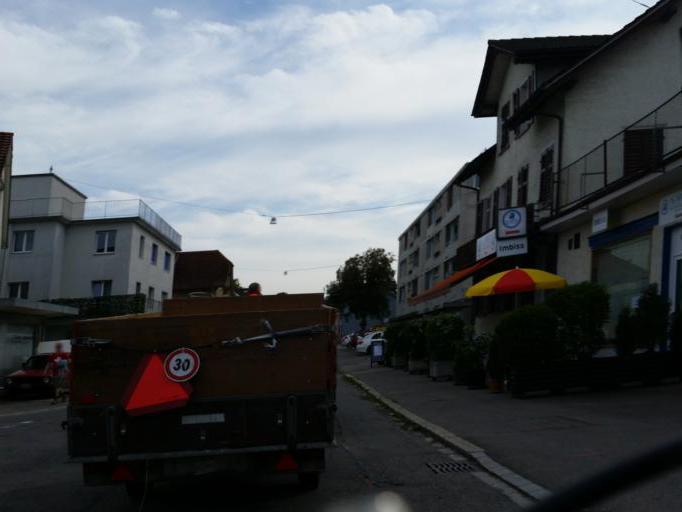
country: CH
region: Thurgau
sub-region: Arbon District
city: Amriswil
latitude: 47.5520
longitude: 9.3050
